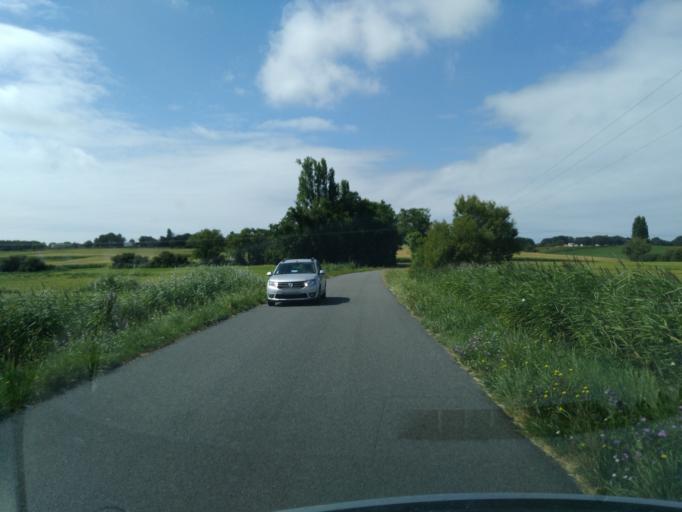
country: FR
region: Poitou-Charentes
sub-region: Departement de la Charente-Maritime
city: Breuillet
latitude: 45.6811
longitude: -1.0823
